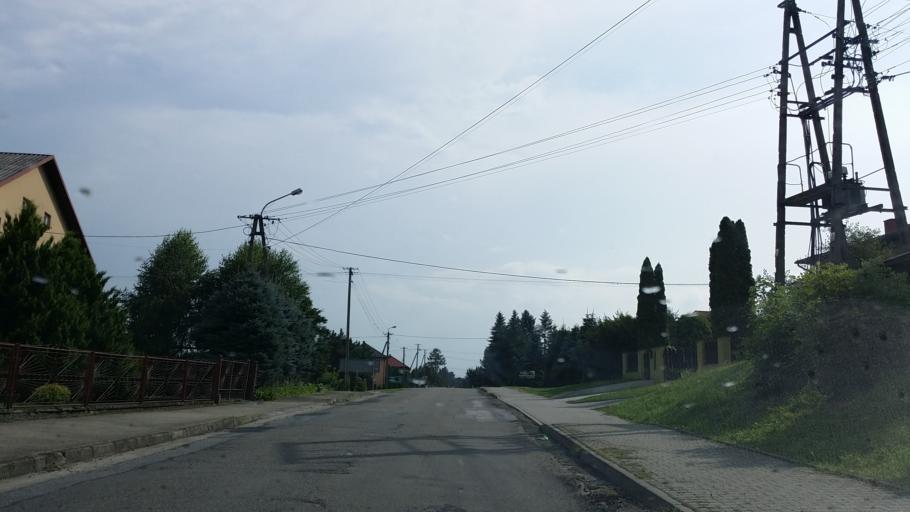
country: PL
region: Lesser Poland Voivodeship
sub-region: Powiat wadowicki
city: Spytkowice
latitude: 49.9931
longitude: 19.5025
